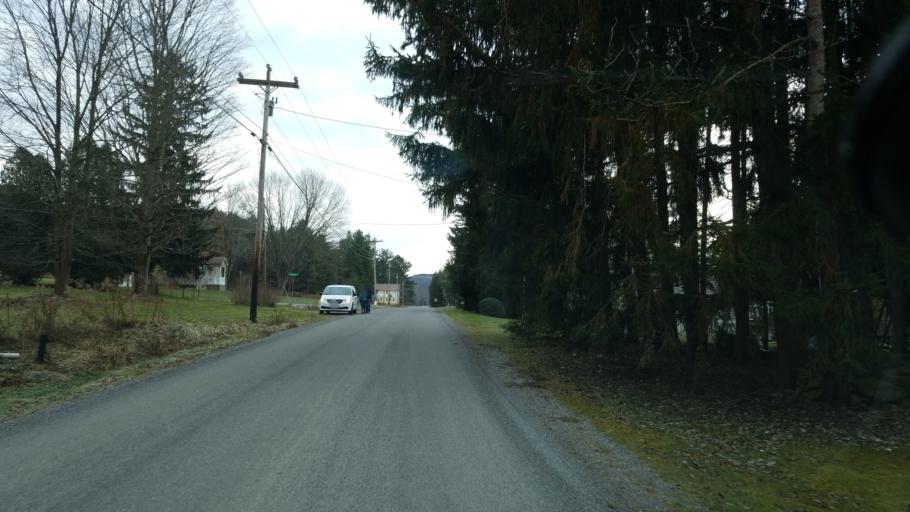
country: US
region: Pennsylvania
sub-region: Clearfield County
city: Treasure Lake
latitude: 41.1105
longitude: -78.6475
